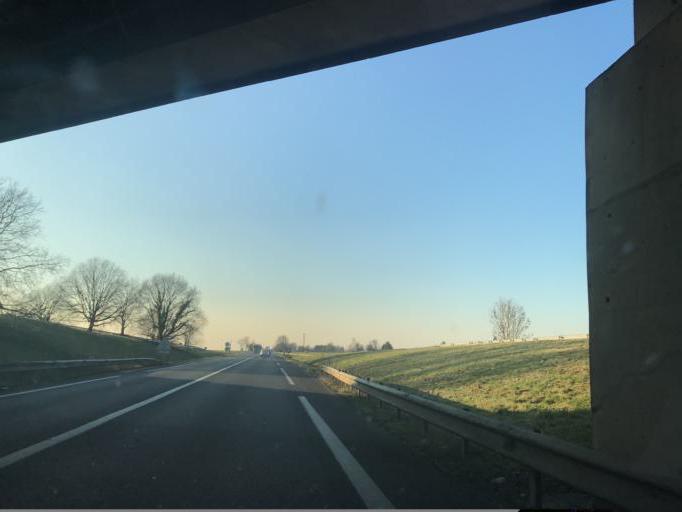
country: FR
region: Ile-de-France
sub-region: Departement de Seine-et-Marne
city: Villiers-sur-Morin
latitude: 48.8556
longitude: 2.8567
